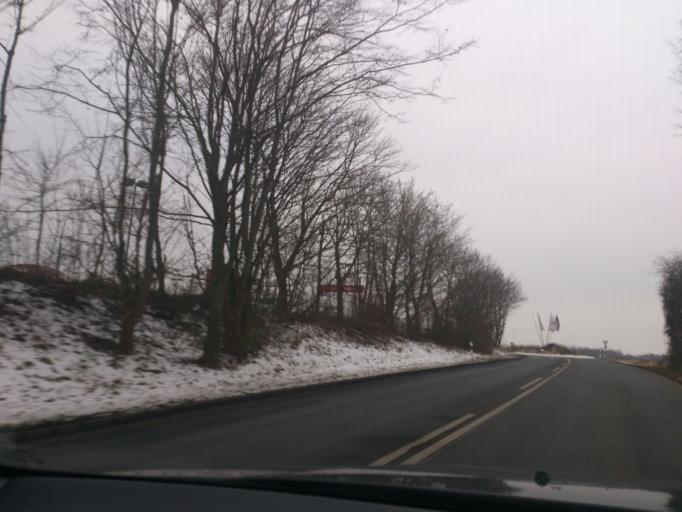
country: DE
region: Bavaria
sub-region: Regierungsbezirk Unterfranken
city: Wuerzburg
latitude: 49.7697
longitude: 9.8637
